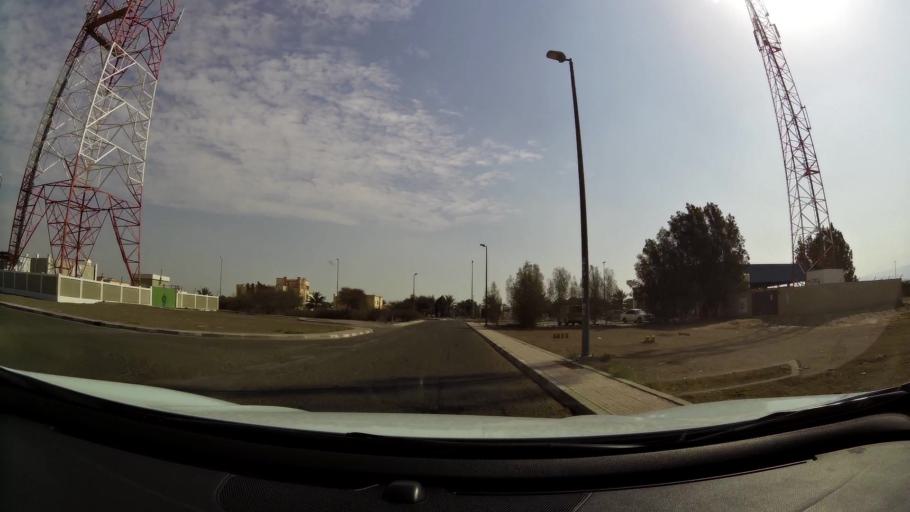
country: AE
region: Abu Dhabi
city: Al Ain
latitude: 24.0946
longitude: 55.9145
